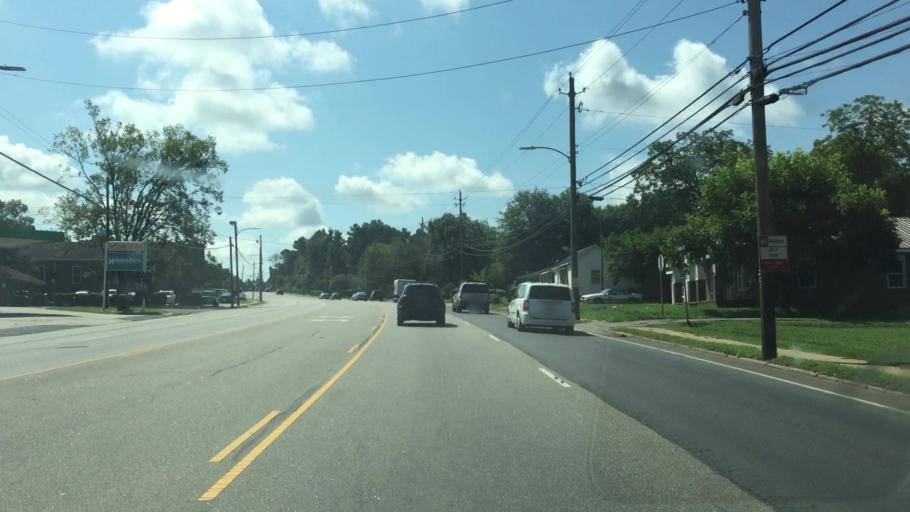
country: US
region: North Carolina
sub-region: Anson County
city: Wadesboro
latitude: 34.9743
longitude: -80.0840
